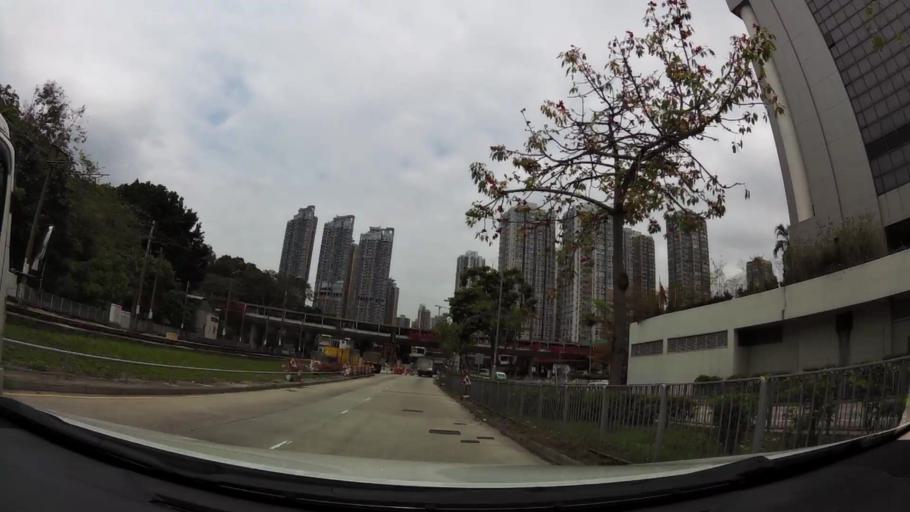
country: HK
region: Tuen Mun
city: Tuen Mun
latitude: 22.3902
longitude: 113.9752
